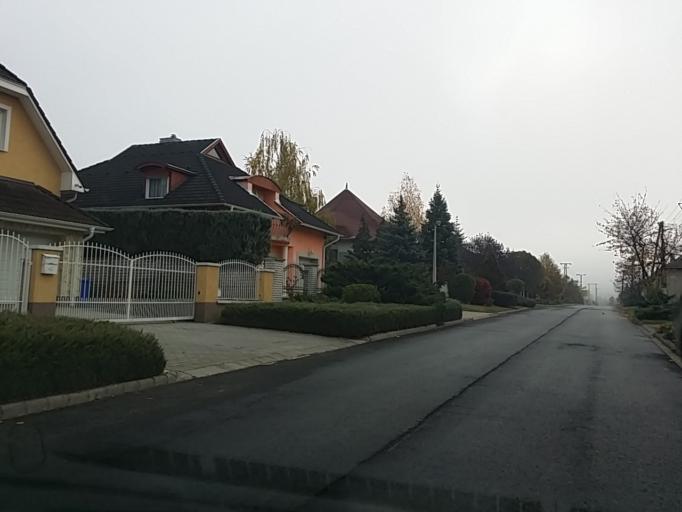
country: HU
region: Heves
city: Gyongyossolymos
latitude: 47.8002
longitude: 19.9336
